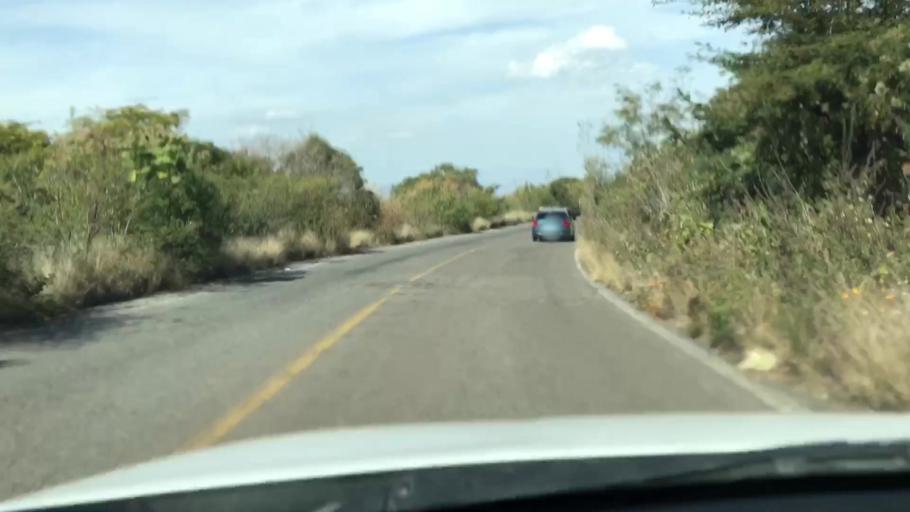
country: MX
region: Jalisco
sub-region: Zacoalco de Torres
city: Barranca de Otates (Barranca de Otatan)
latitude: 20.2270
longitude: -103.6894
